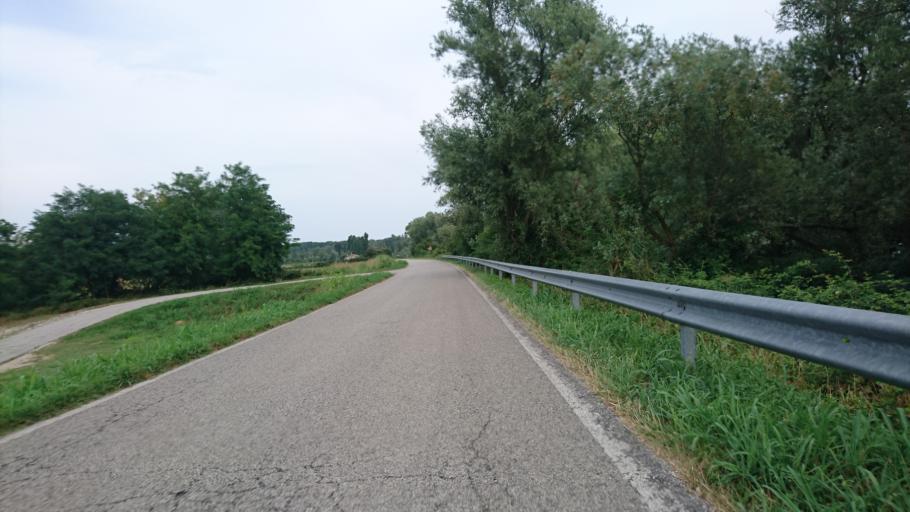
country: IT
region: Veneto
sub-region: Provincia di Venezia
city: Sant'Anna
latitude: 45.1439
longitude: 12.2962
